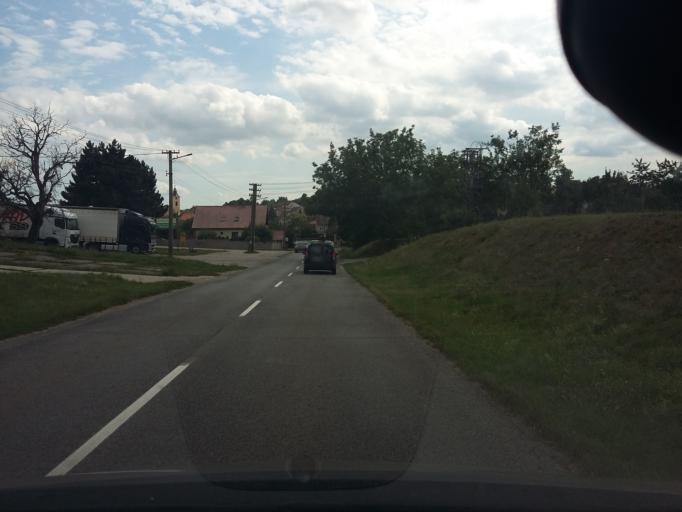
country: SK
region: Trnavsky
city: Gbely
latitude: 48.7259
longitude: 17.1618
